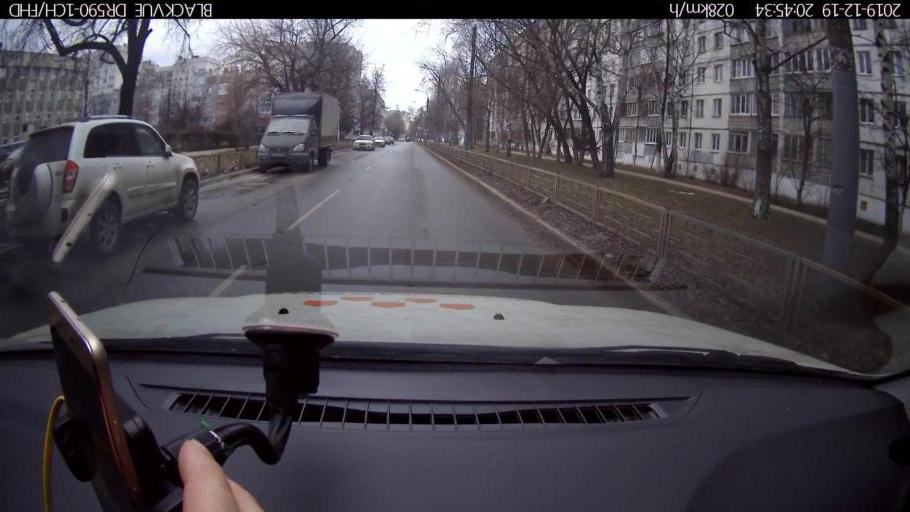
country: RU
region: Nizjnij Novgorod
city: Nizhniy Novgorod
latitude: 56.3295
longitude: 43.8741
